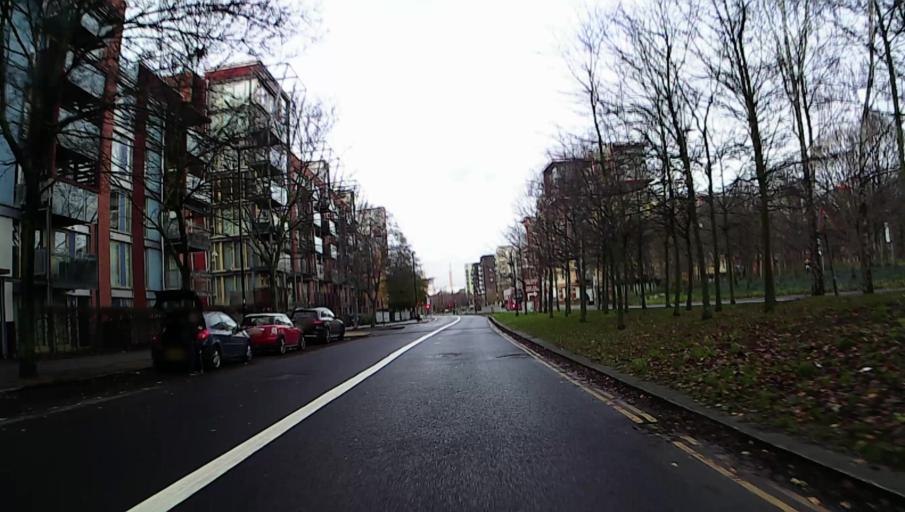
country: GB
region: England
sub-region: Greater London
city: Blackheath
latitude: 51.4931
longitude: 0.0144
